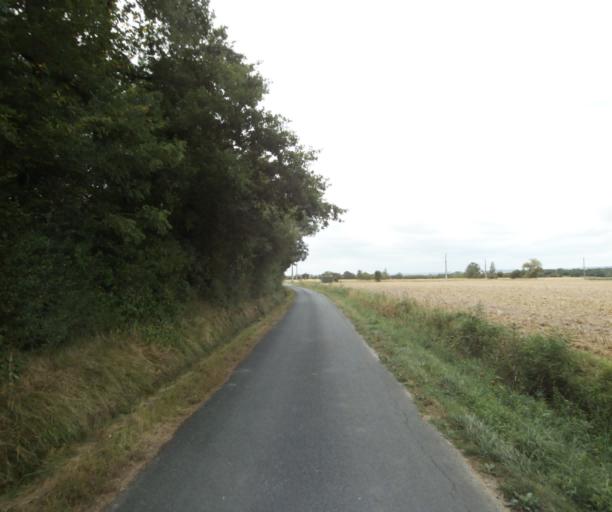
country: FR
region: Midi-Pyrenees
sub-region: Departement du Tarn
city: Soreze
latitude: 43.4701
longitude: 2.0419
